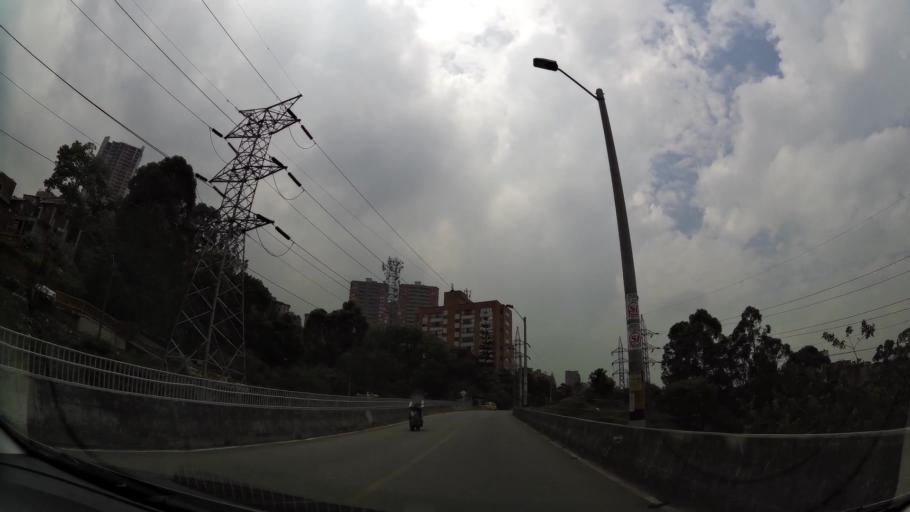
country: CO
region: Antioquia
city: Medellin
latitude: 6.2310
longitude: -75.5640
